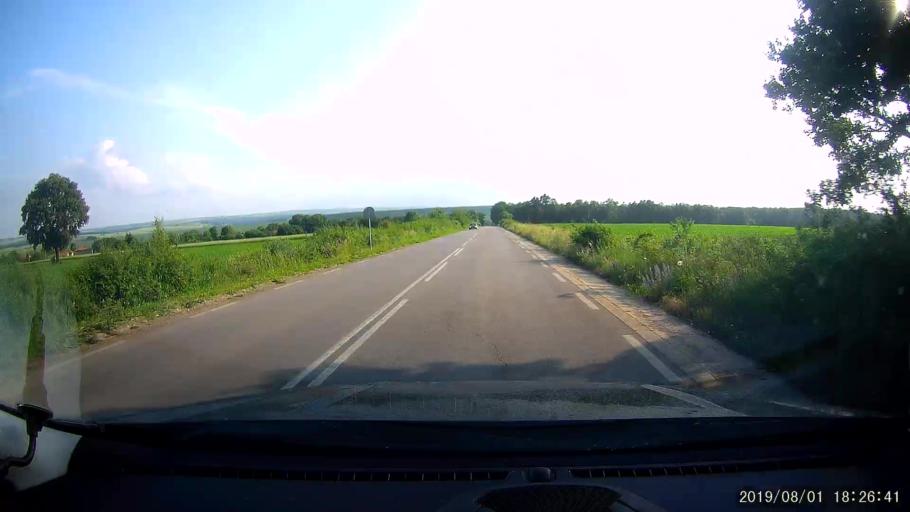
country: BG
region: Shumen
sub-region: Obshtina Venets
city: Venets
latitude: 43.5972
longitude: 26.9878
